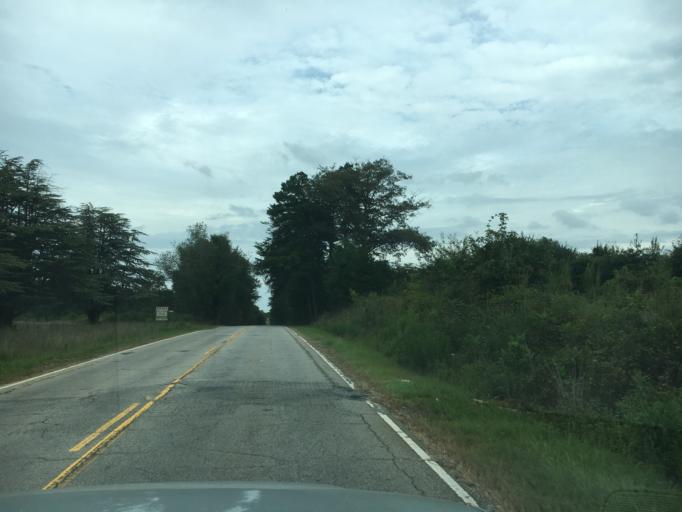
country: US
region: South Carolina
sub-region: Spartanburg County
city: Duncan
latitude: 34.9365
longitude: -82.1814
